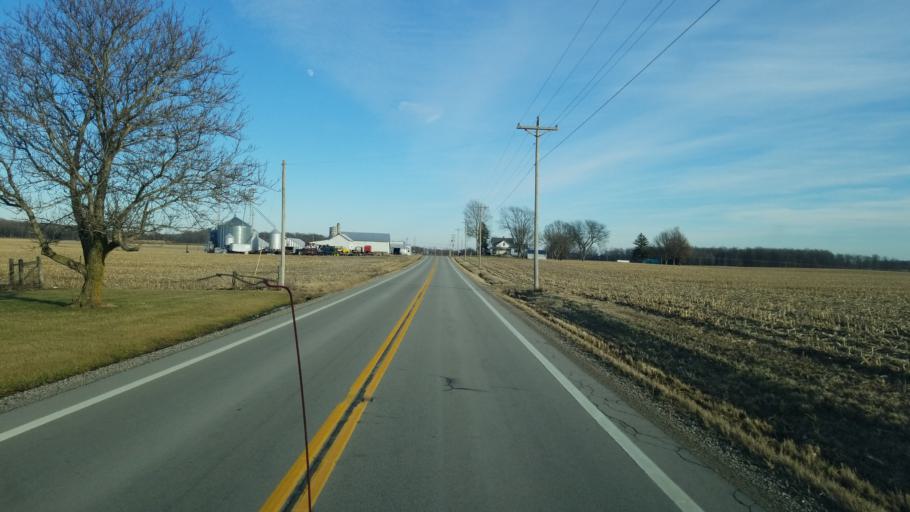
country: US
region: Ohio
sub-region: Huron County
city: Greenwich
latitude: 41.1030
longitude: -82.5476
